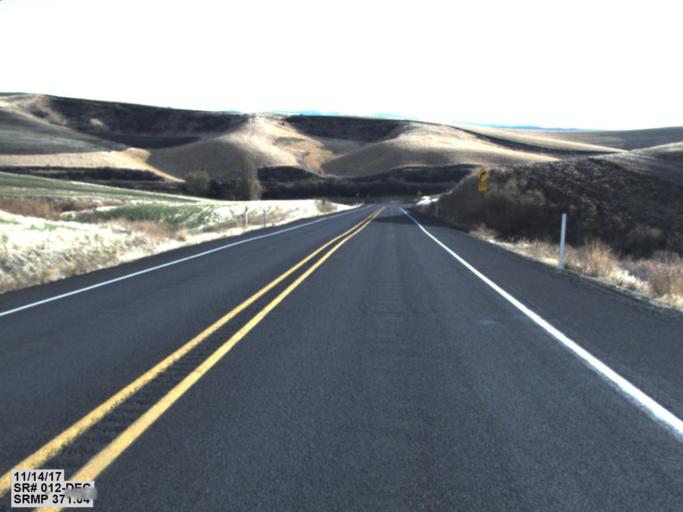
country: US
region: Washington
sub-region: Columbia County
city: Dayton
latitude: 46.3605
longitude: -117.9507
